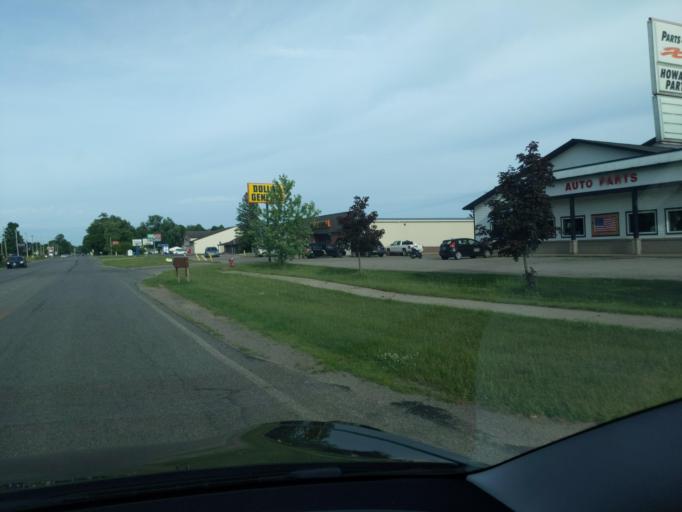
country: US
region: Michigan
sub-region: Montcalm County
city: Howard City
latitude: 43.3957
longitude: -85.4858
